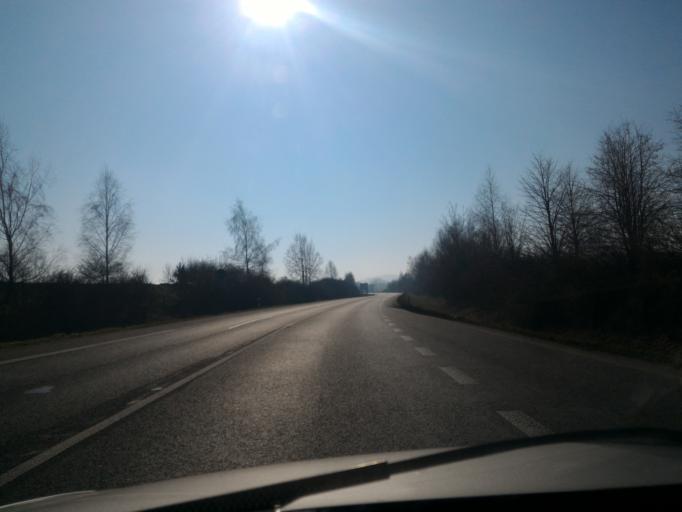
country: CZ
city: Hradek nad Nisou
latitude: 50.8635
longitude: 14.8521
